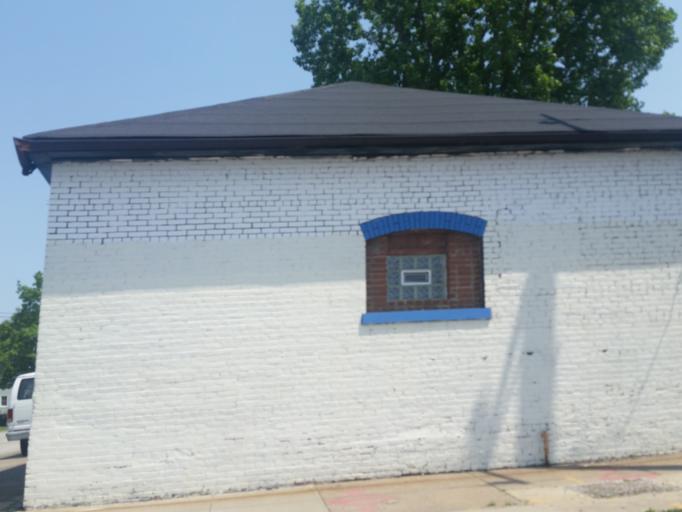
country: US
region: Ohio
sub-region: Cuyahoga County
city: Newburgh Heights
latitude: 41.4903
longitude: -81.6335
